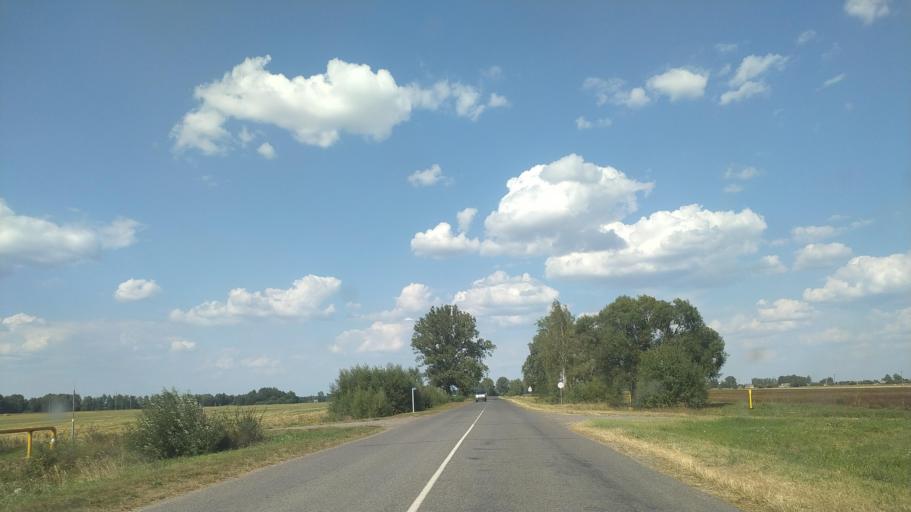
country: BY
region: Brest
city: Drahichyn
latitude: 52.1249
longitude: 25.1171
